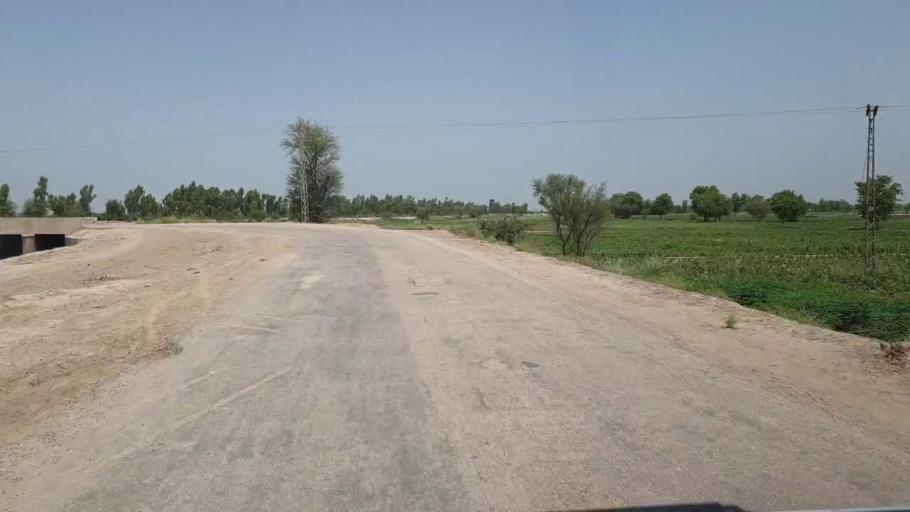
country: PK
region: Sindh
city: Nawabshah
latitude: 26.3435
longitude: 68.3842
